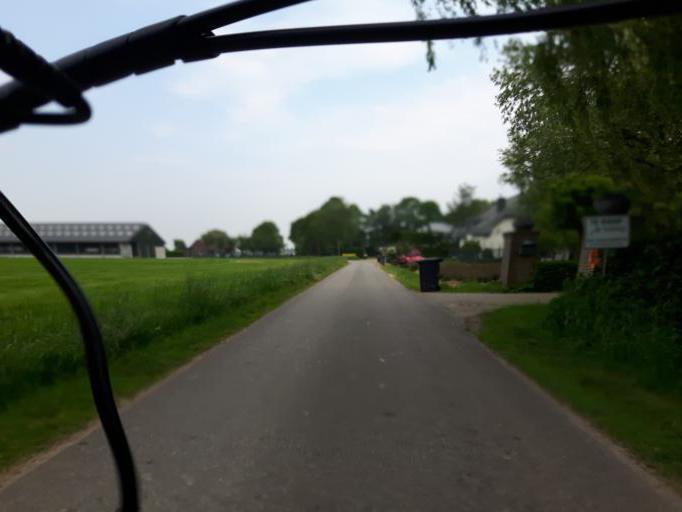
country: NL
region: North Brabant
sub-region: Gemeente Steenbergen
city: Welberg
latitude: 51.5529
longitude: 4.3421
